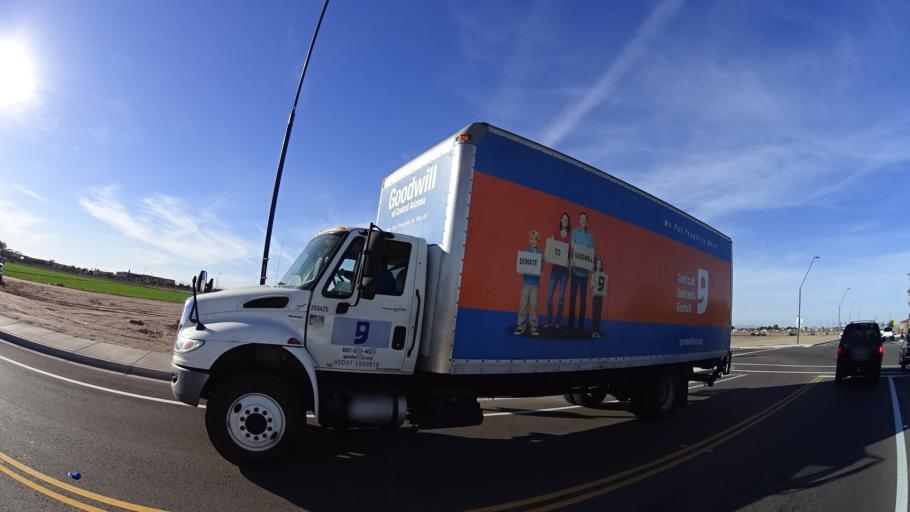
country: US
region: Arizona
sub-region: Maricopa County
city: Queen Creek
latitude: 33.2607
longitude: -111.6346
